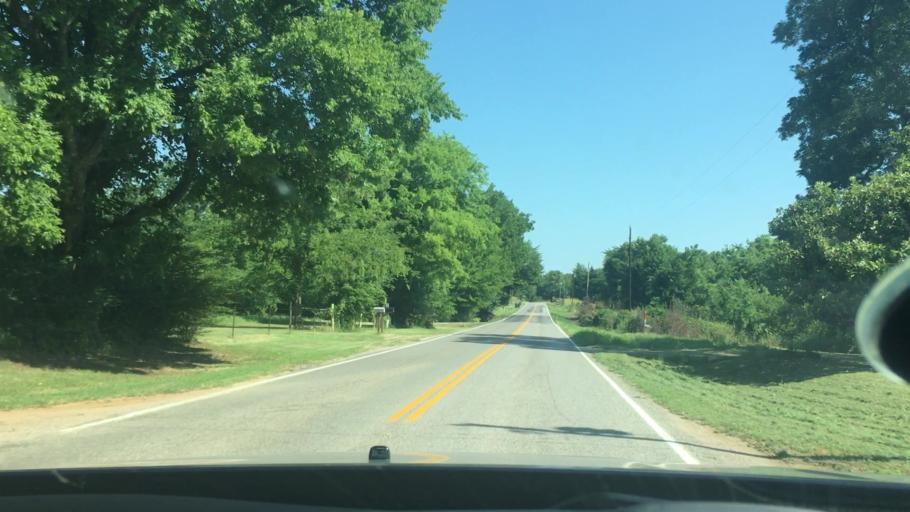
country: US
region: Oklahoma
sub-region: Johnston County
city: Tishomingo
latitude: 34.2035
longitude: -96.5428
